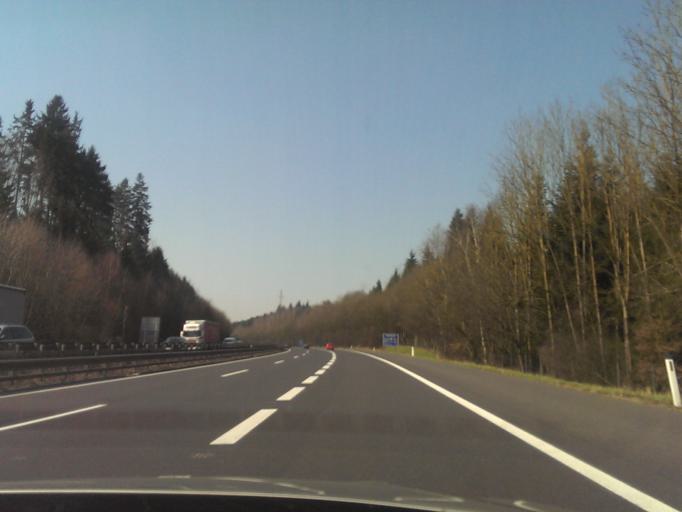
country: AT
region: Upper Austria
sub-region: Wels-Land
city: Gunskirchen
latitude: 48.1833
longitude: 13.9754
